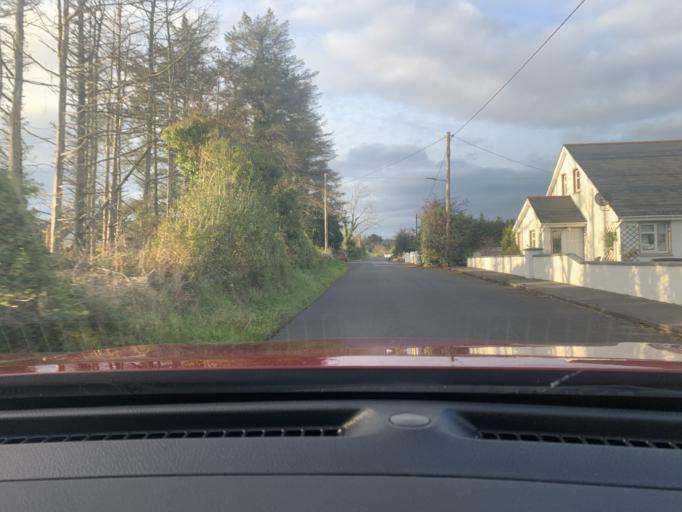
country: IE
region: Connaught
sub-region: Roscommon
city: Ballaghaderreen
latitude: 53.9071
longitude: -8.5788
